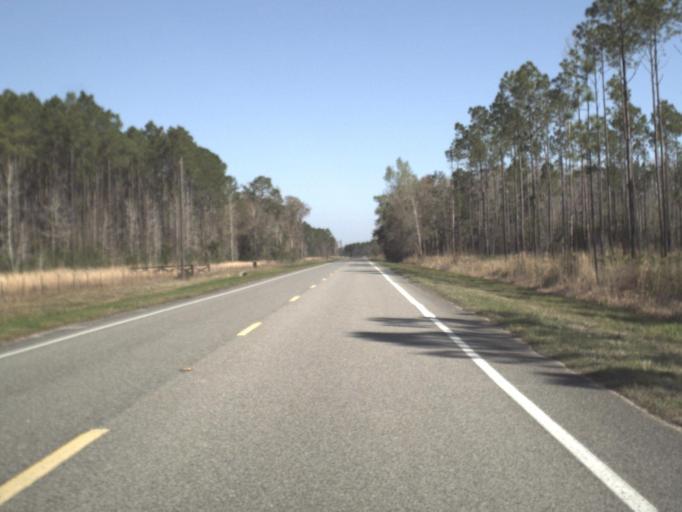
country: US
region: Florida
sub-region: Leon County
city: Woodville
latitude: 30.2598
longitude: -84.0424
